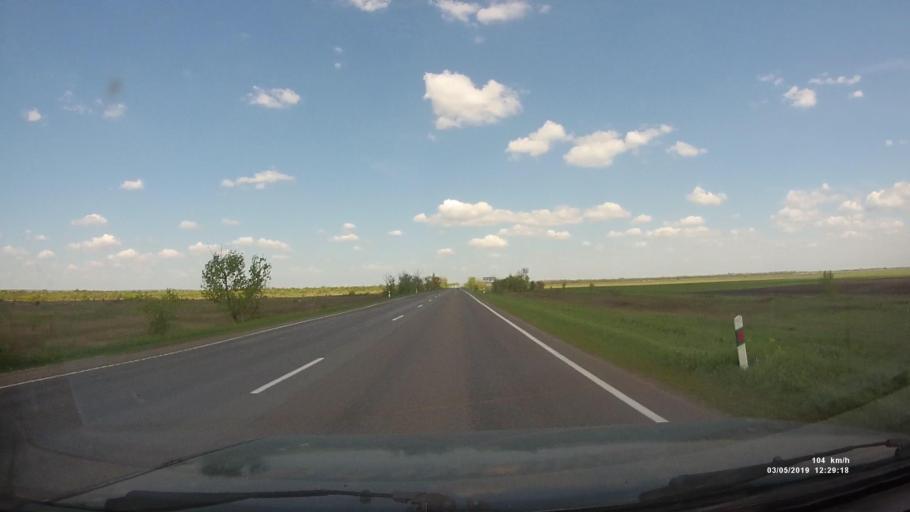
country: RU
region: Rostov
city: Semikarakorsk
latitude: 47.4856
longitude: 40.7354
